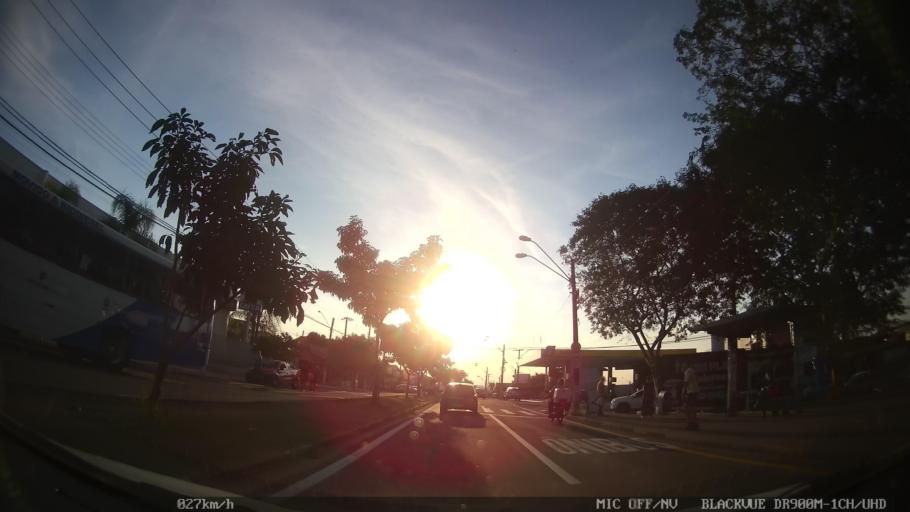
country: BR
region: Sao Paulo
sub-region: Campinas
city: Campinas
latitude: -22.9681
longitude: -47.1285
